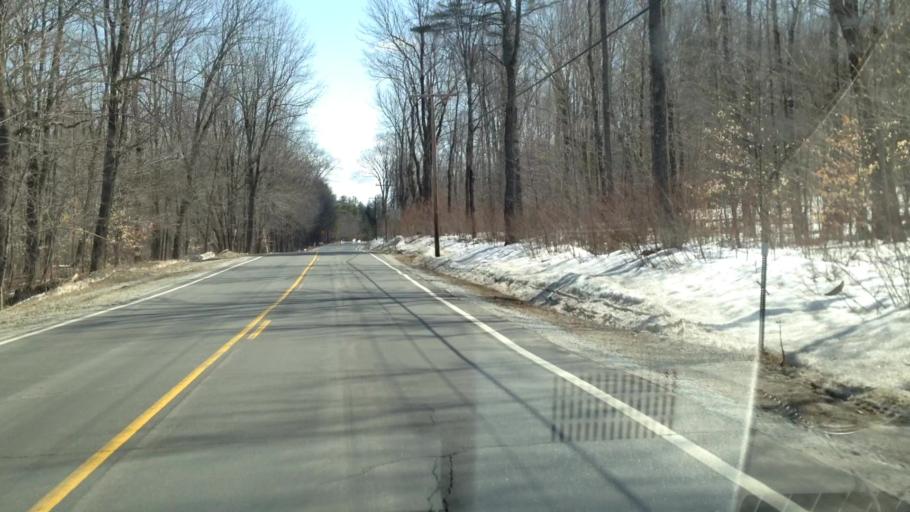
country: US
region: New Hampshire
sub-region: Merrimack County
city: Wilmot
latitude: 43.4600
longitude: -71.9390
